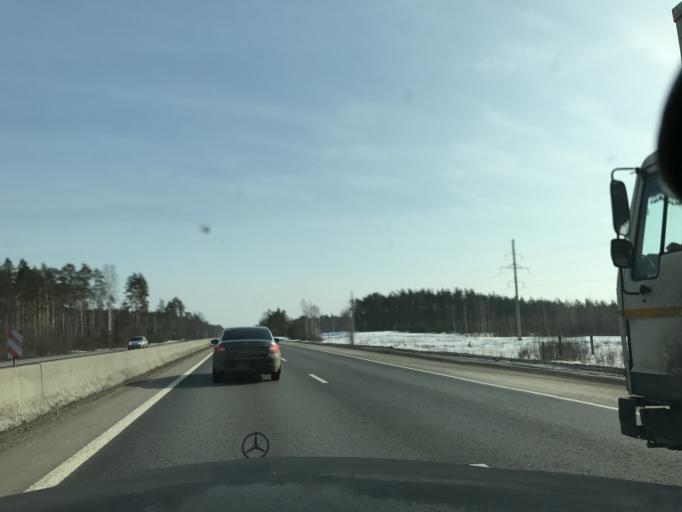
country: RU
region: Nizjnij Novgorod
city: Yuganets
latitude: 56.2897
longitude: 43.2710
